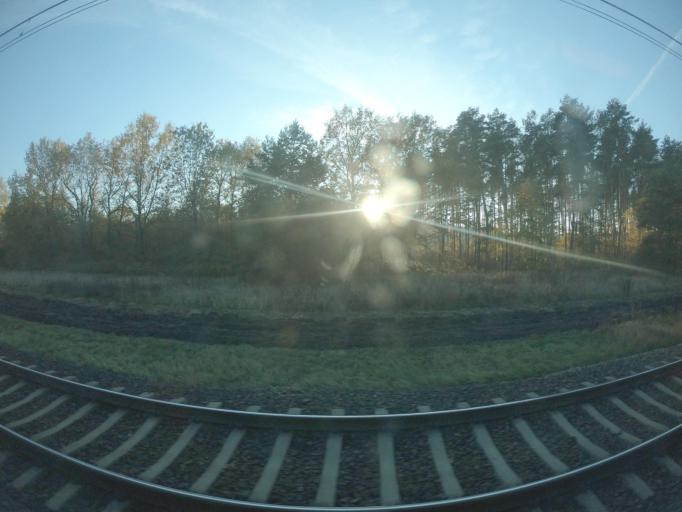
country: PL
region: Lubusz
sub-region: Powiat slubicki
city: Rzepin
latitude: 52.2628
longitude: 14.9405
